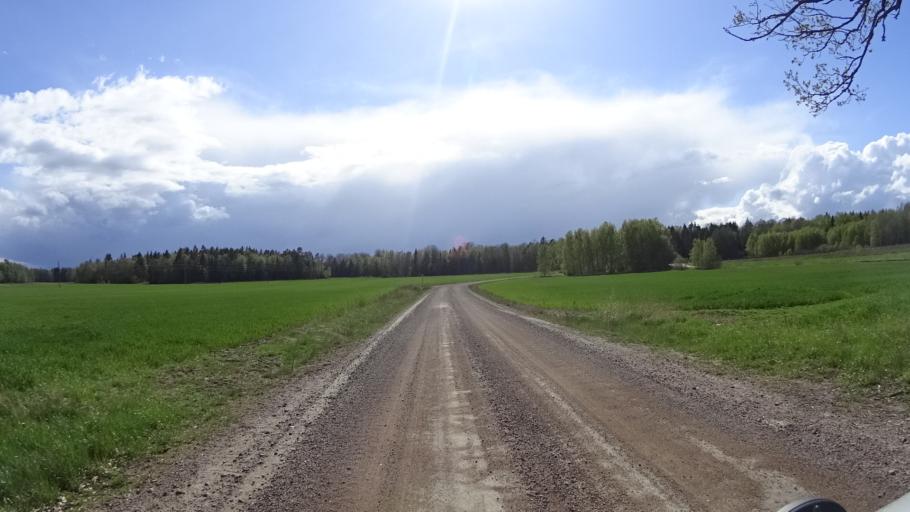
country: SE
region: Vaestra Goetaland
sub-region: Karlsborgs Kommun
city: Karlsborg
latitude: 58.4996
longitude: 14.4660
